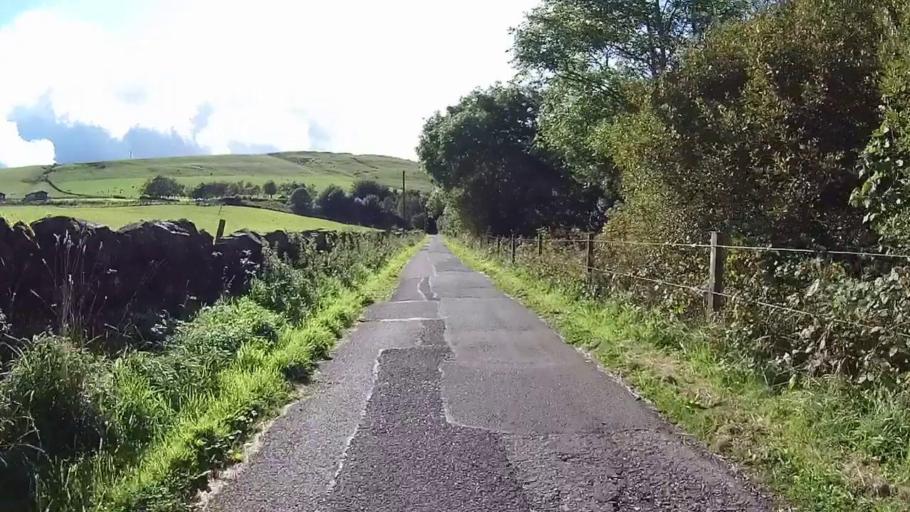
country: GB
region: Scotland
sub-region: Fife
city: Ballingry
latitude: 56.1796
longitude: -3.3342
